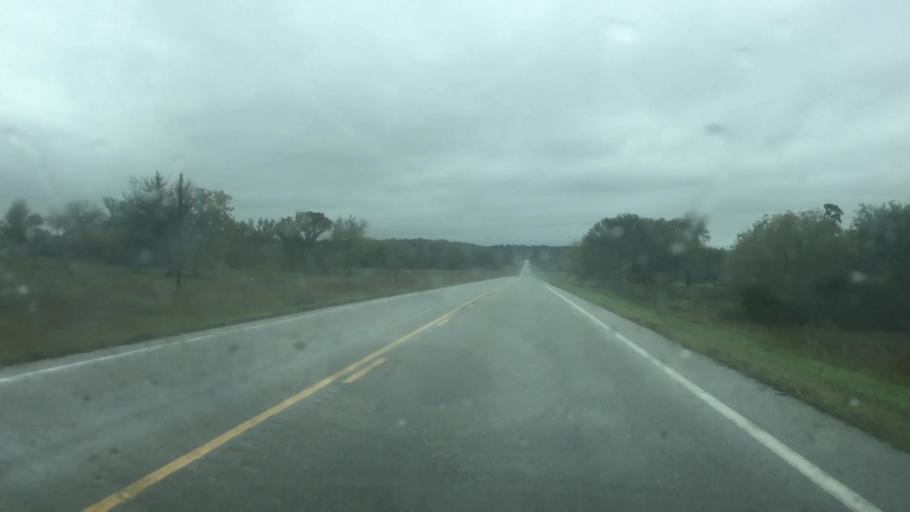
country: US
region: Kansas
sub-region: Anderson County
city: Garnett
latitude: 38.3843
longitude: -95.1108
